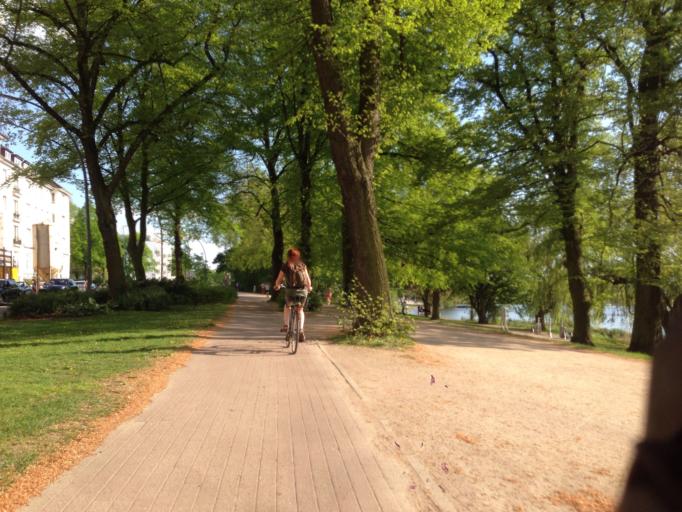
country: DE
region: Hamburg
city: Hamburg
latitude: 53.5670
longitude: 10.0163
